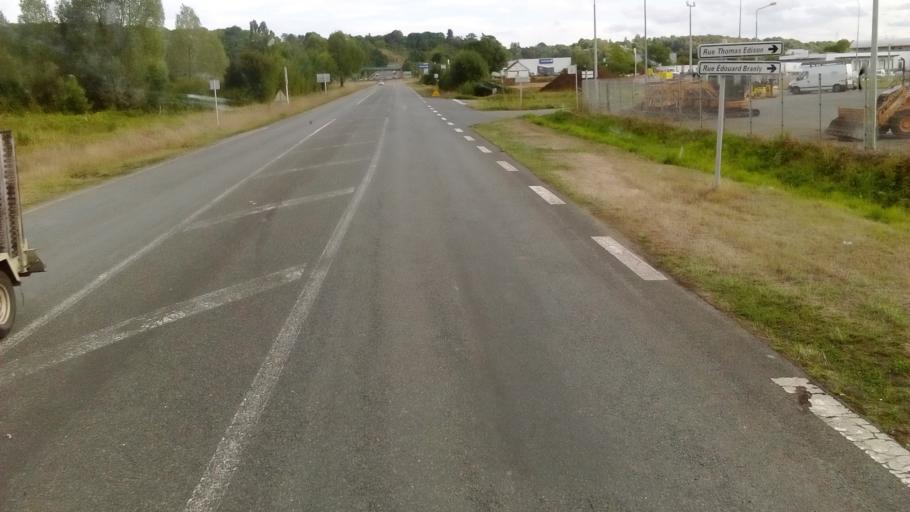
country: FR
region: Bourgogne
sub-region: Departement de la Nievre
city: Varennes-Vauzelles
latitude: 47.0481
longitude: 3.1304
